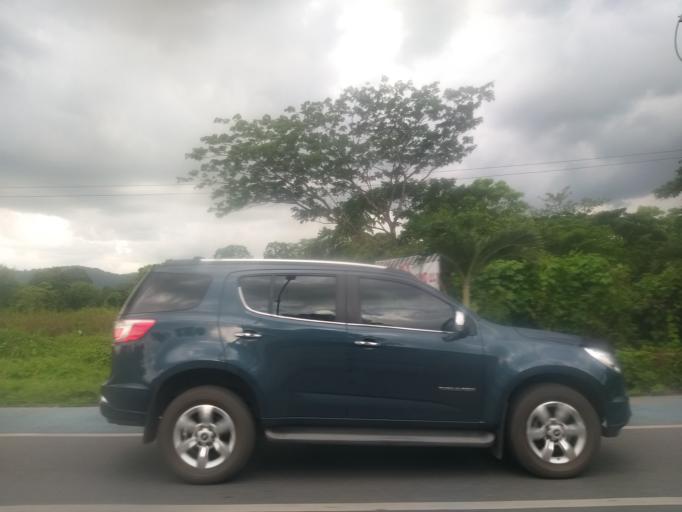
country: TH
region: Nakhon Nayok
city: Nakhon Nayok
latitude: 14.3215
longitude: 101.3118
